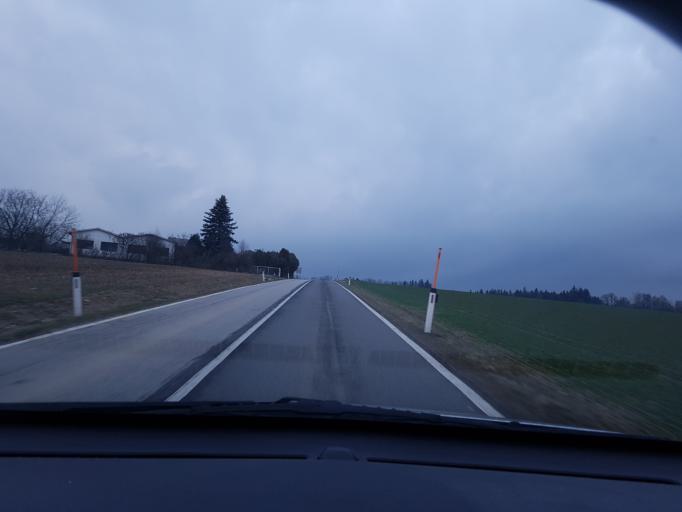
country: AT
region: Upper Austria
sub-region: Politischer Bezirk Steyr-Land
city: Sierning
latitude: 48.1202
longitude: 14.3473
